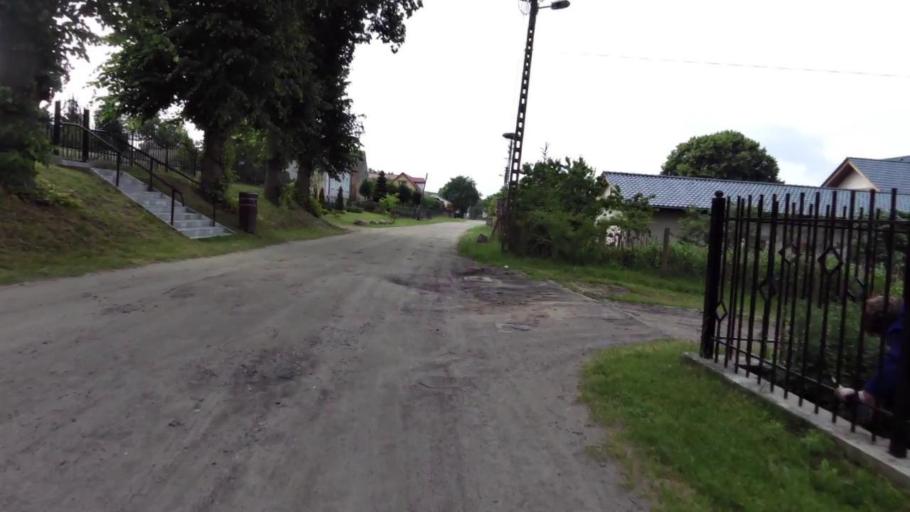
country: PL
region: West Pomeranian Voivodeship
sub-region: Powiat kamienski
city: Wolin
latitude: 53.8101
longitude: 14.6146
